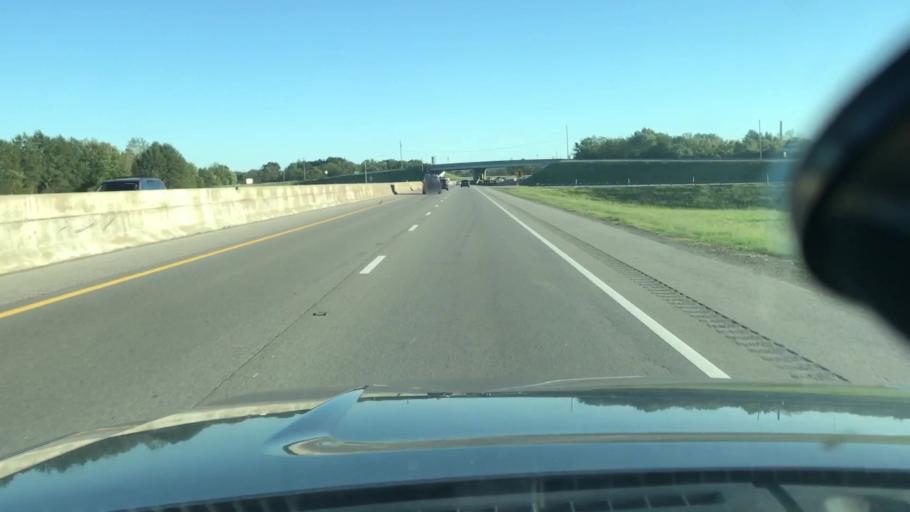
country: US
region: Tennessee
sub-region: Davidson County
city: Nashville
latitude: 36.1908
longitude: -86.8640
